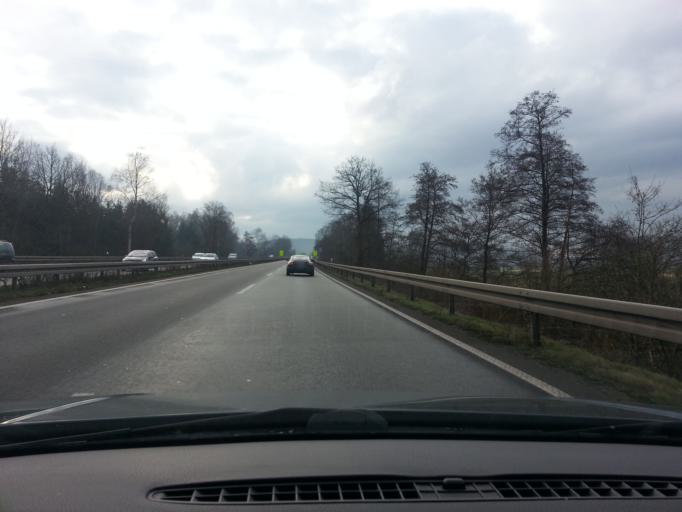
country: DE
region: Saarland
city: Homburg
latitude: 49.2799
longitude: 7.3128
